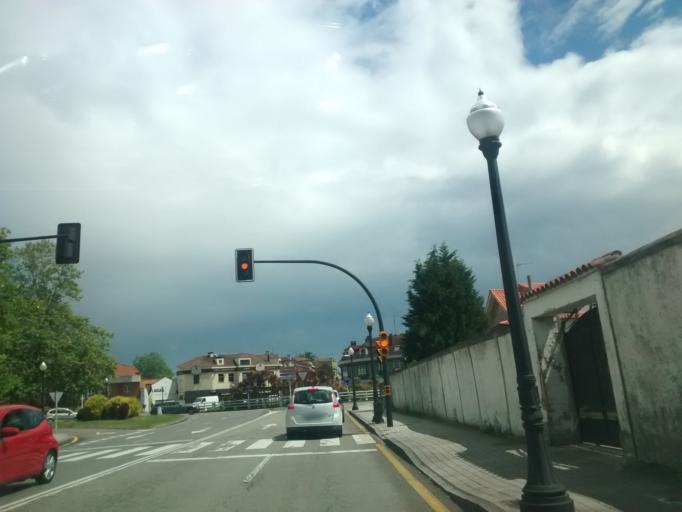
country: ES
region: Asturias
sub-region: Province of Asturias
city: Gijon
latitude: 43.5340
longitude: -5.6359
